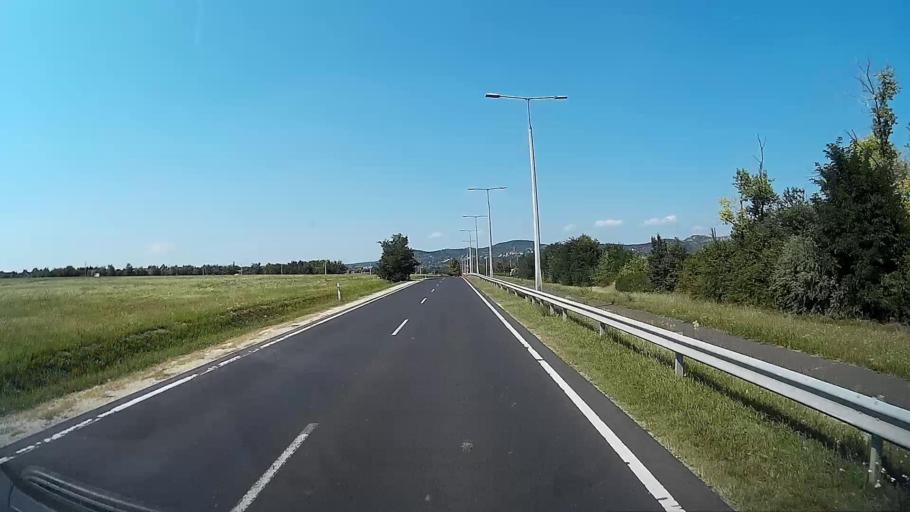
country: HU
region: Pest
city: Toeroekbalint
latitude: 47.4371
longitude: 18.9352
